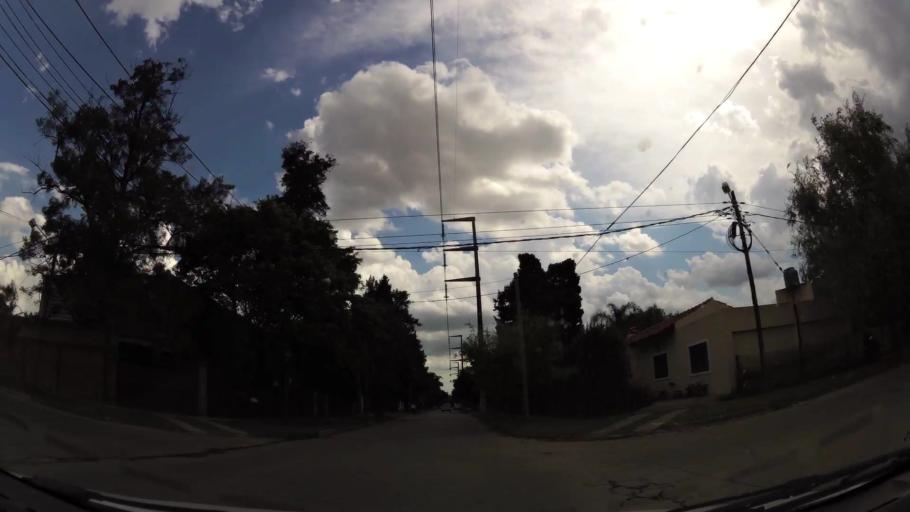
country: AR
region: Buenos Aires
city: Ituzaingo
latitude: -34.6346
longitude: -58.6796
